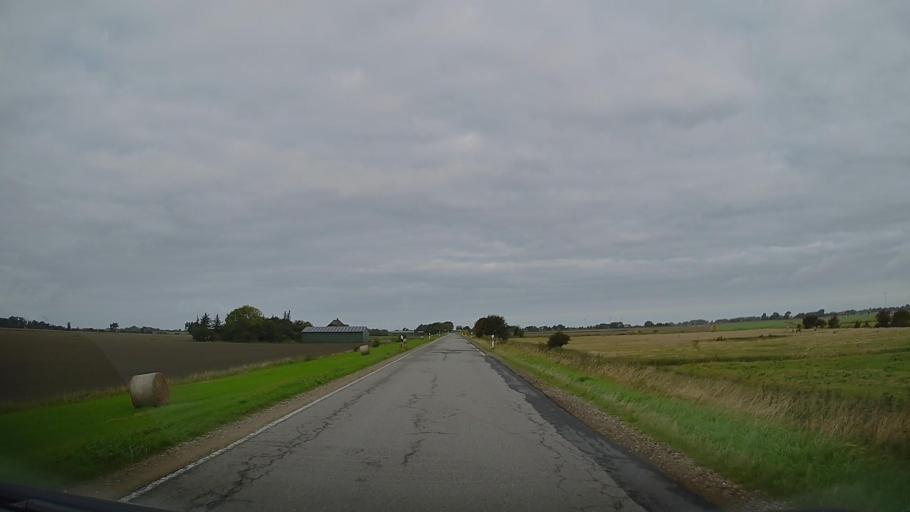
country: DE
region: Schleswig-Holstein
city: Emmelsbull-Horsbull
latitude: 54.7915
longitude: 8.7262
